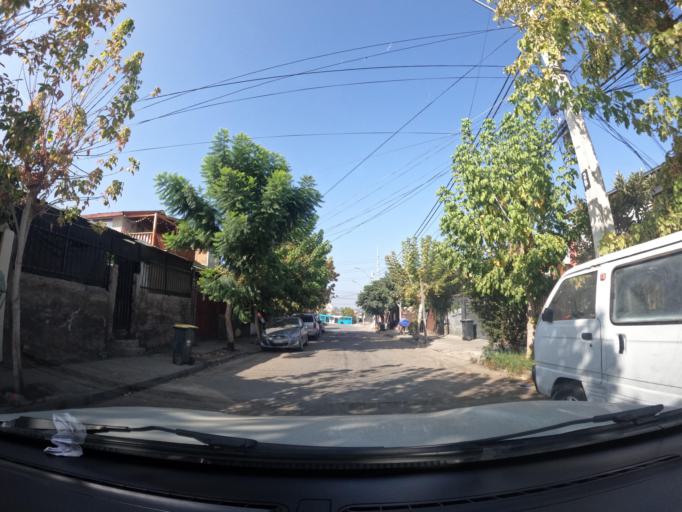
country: CL
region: Santiago Metropolitan
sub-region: Provincia de Santiago
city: Villa Presidente Frei, Nunoa, Santiago, Chile
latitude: -33.4775
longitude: -70.5302
